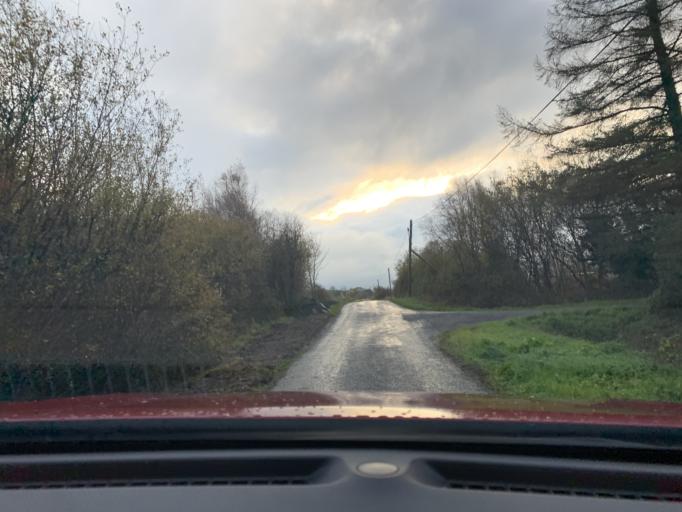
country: IE
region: Connaught
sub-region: Sligo
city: Ballymote
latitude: 54.0315
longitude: -8.5298
